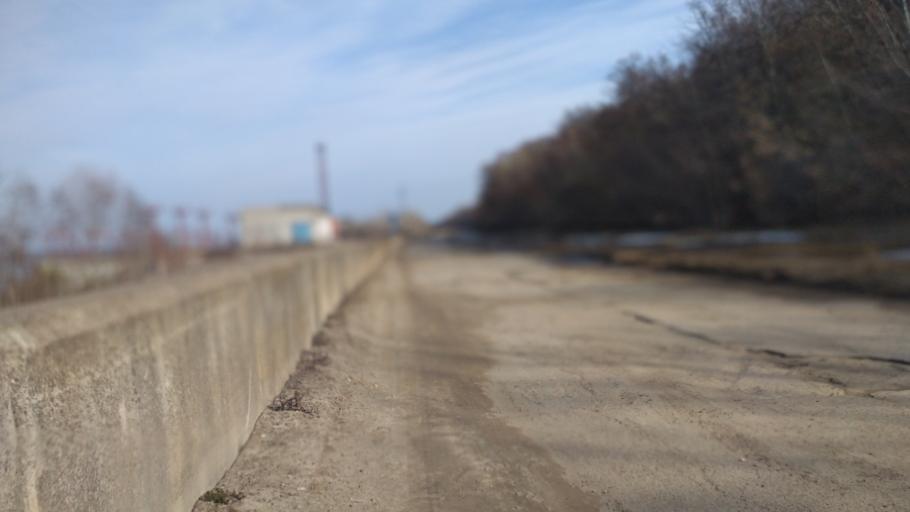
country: RU
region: Chuvashia
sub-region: Cheboksarskiy Rayon
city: Cheboksary
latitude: 56.1474
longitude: 47.3006
